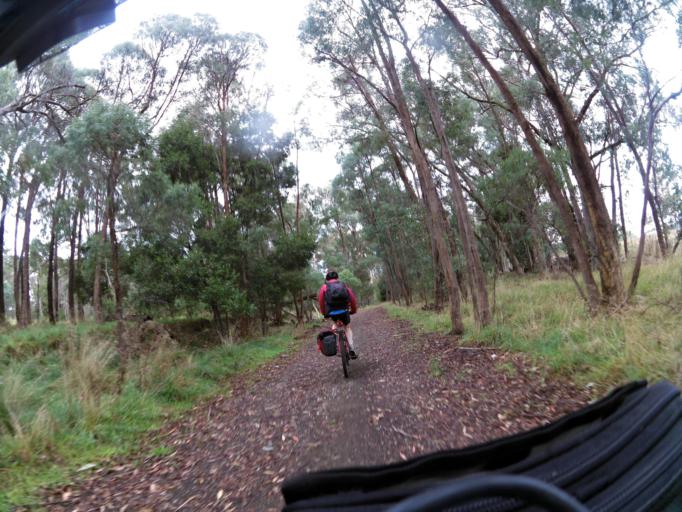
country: AU
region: New South Wales
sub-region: Greater Hume Shire
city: Holbrook
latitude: -36.1573
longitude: 147.4854
